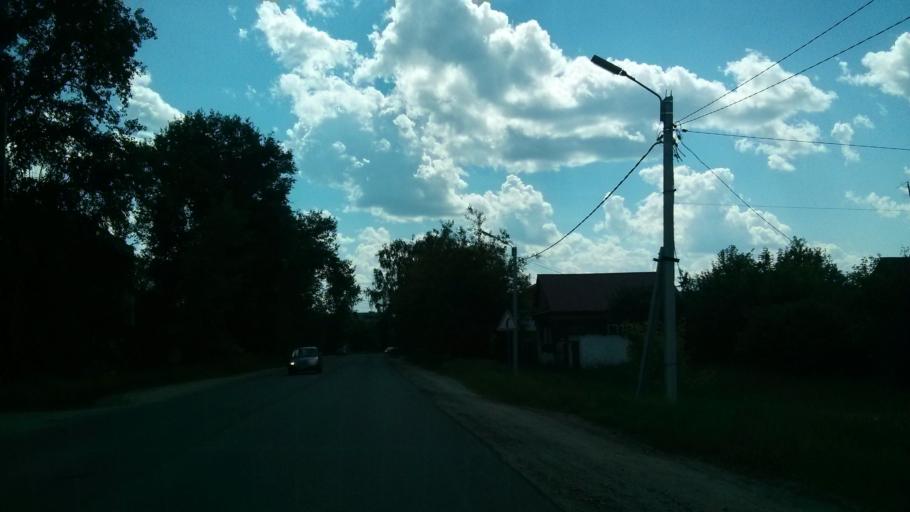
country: RU
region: Vladimir
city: Murom
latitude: 55.5364
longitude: 41.9761
